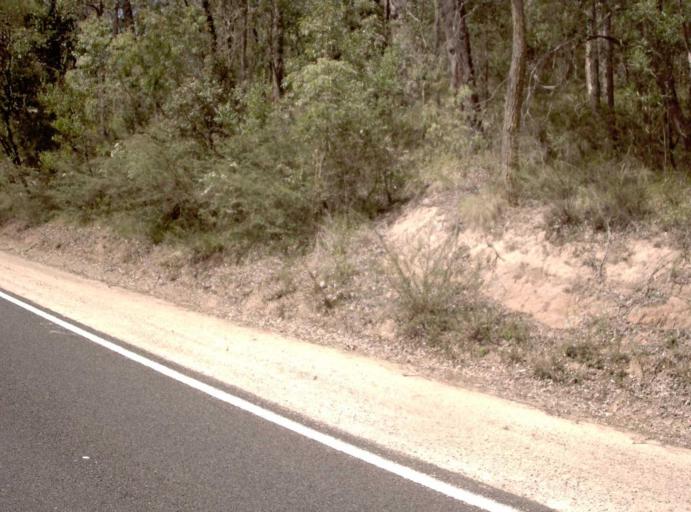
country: AU
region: New South Wales
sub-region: Bega Valley
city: Eden
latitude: -37.4337
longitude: 149.6450
